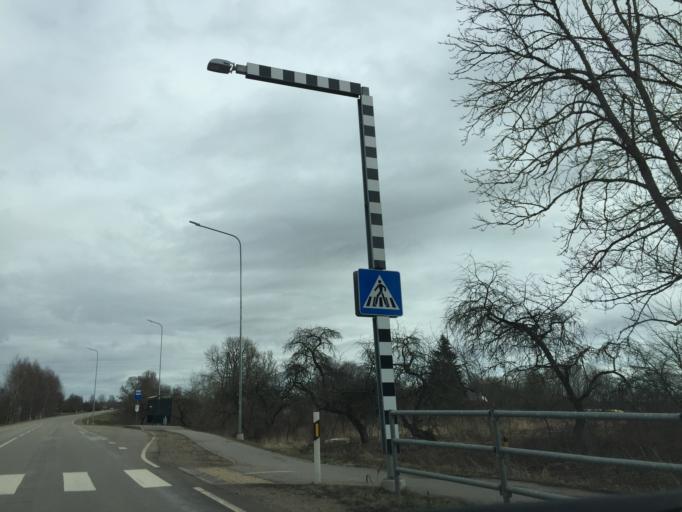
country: LV
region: Daugavpils
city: Daugavpils
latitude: 55.9106
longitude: 26.6574
